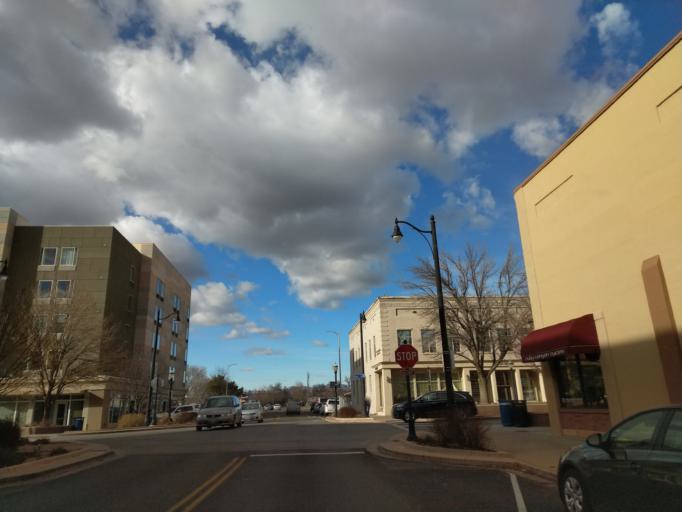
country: US
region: Colorado
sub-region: Mesa County
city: Grand Junction
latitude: 39.0670
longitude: -108.5678
